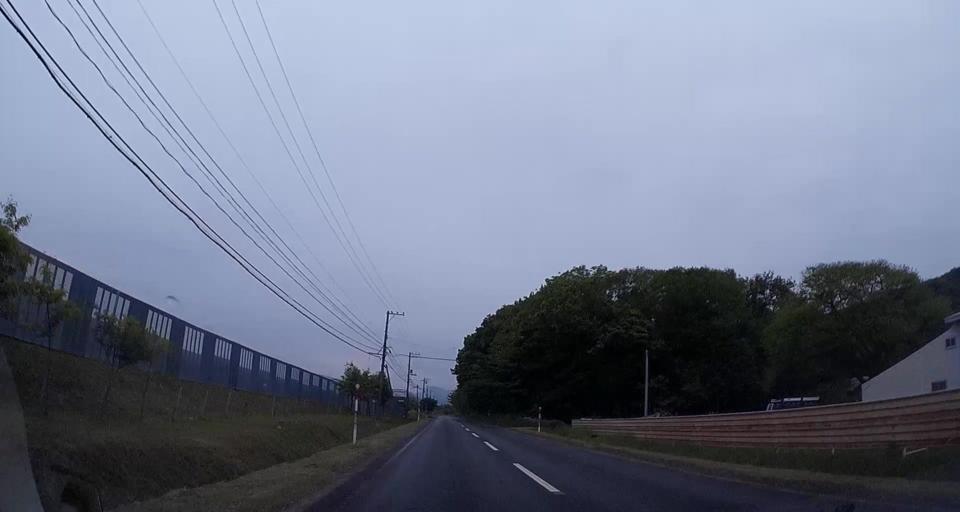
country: JP
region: Hokkaido
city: Shiraoi
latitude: 42.5883
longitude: 141.3094
